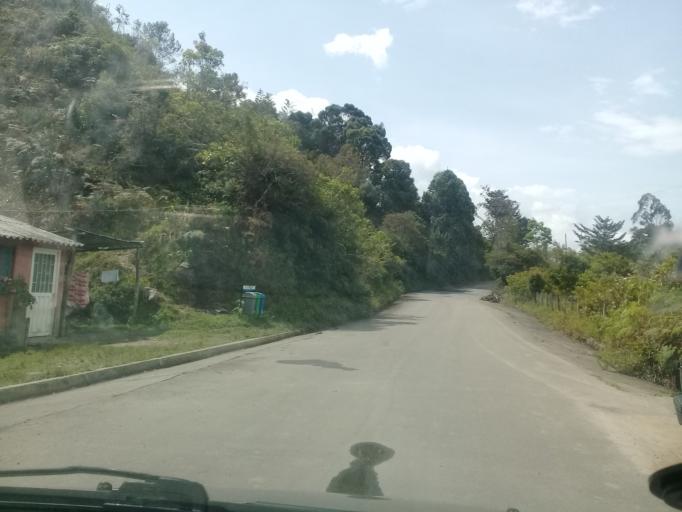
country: CO
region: Cundinamarca
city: Gachala
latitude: 4.6993
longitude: -73.4786
